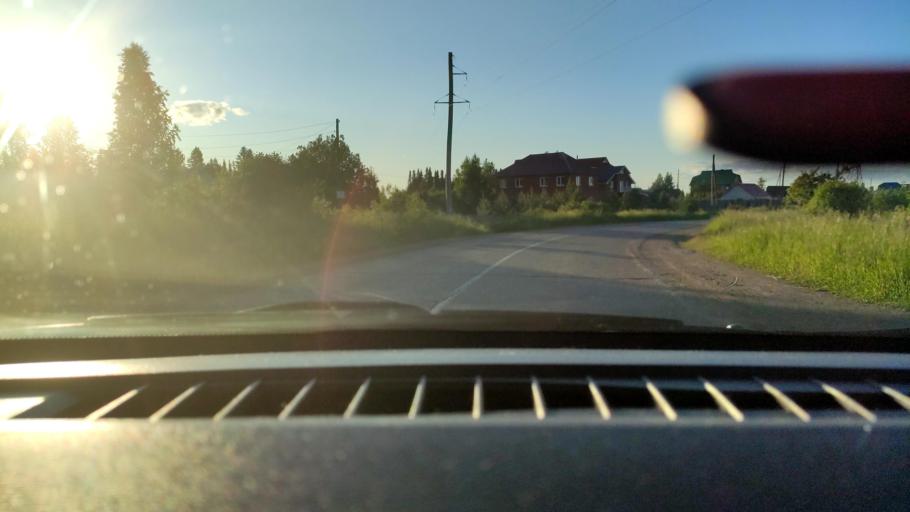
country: RU
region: Perm
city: Kultayevo
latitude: 57.9297
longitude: 55.8627
